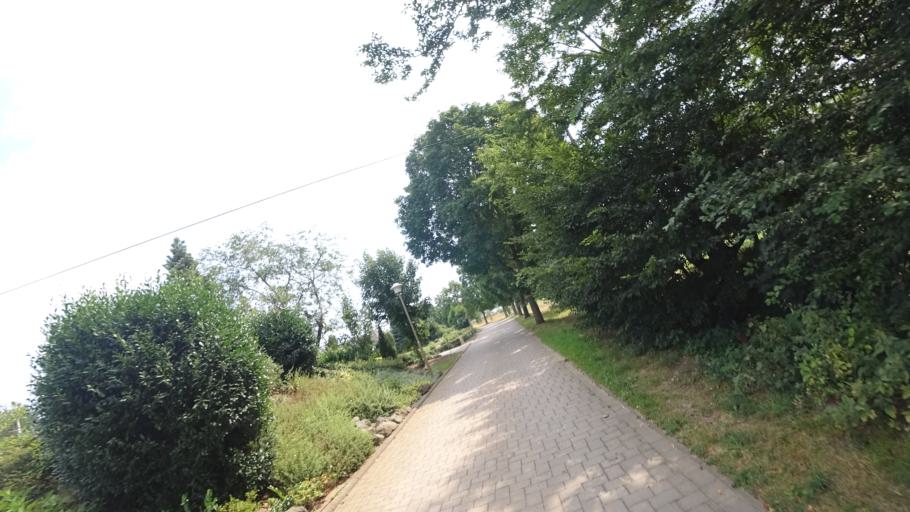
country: DE
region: Rheinland-Pfalz
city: Simmern
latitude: 50.4126
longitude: 7.6801
